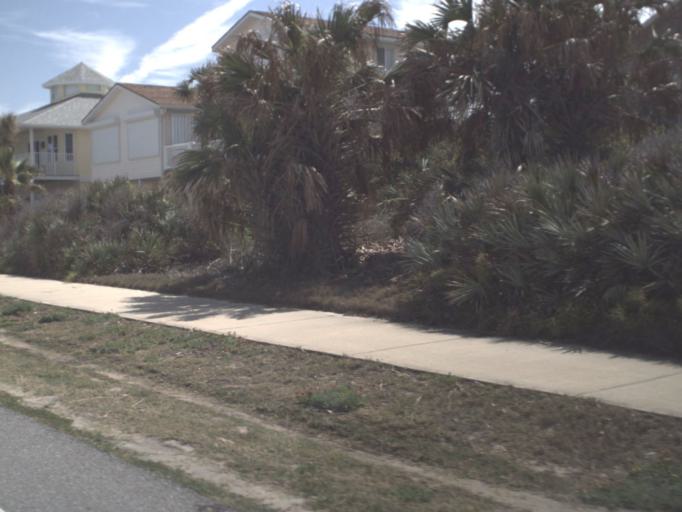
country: US
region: Florida
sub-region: Flagler County
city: Flagler Beach
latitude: 29.4463
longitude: -81.1113
